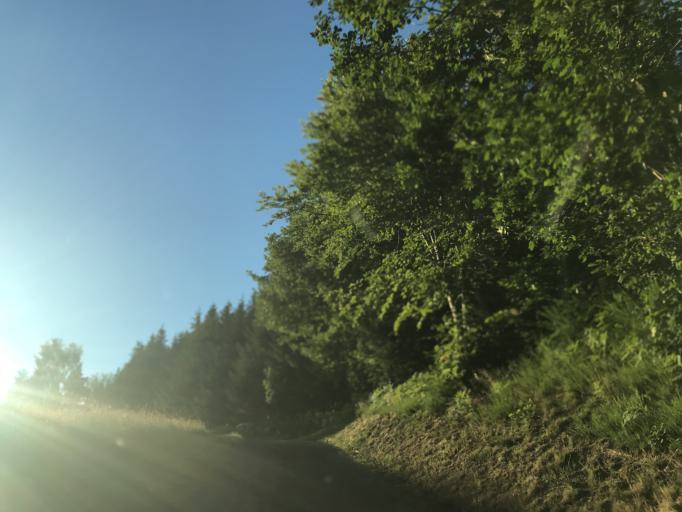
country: FR
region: Auvergne
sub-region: Departement du Puy-de-Dome
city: Celles-sur-Durolle
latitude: 45.7915
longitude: 3.6779
